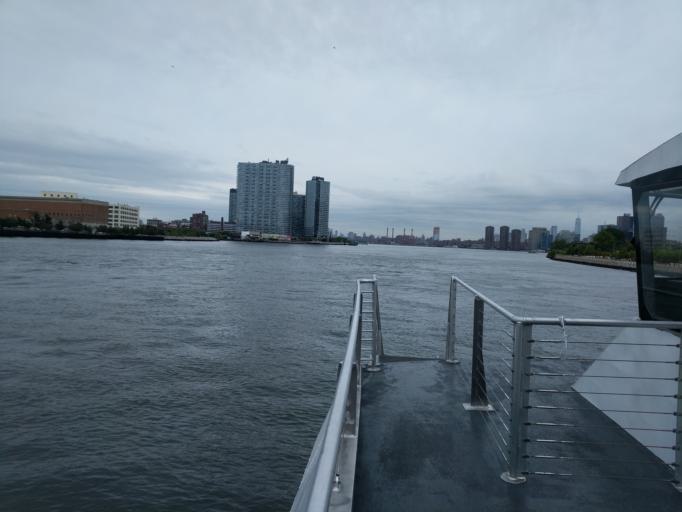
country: US
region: New York
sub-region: Queens County
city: Long Island City
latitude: 40.7554
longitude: -73.9538
